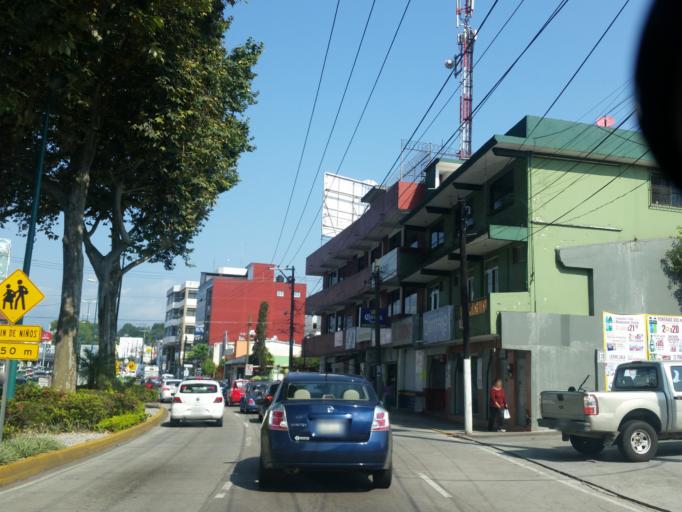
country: MX
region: Veracruz
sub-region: Xalapa
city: Xalapa de Enriquez
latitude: 19.5215
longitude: -96.9065
